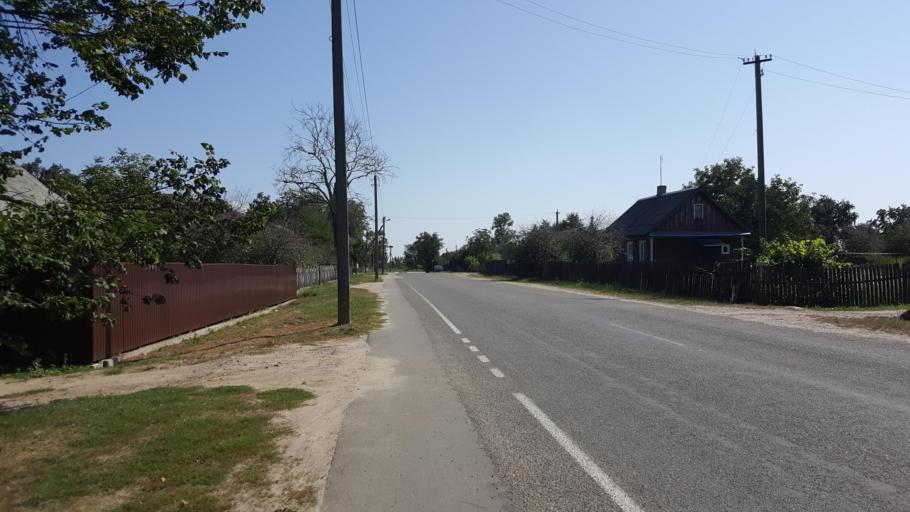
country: PL
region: Podlasie
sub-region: Powiat hajnowski
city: Czeremcha
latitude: 52.4724
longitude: 23.5088
